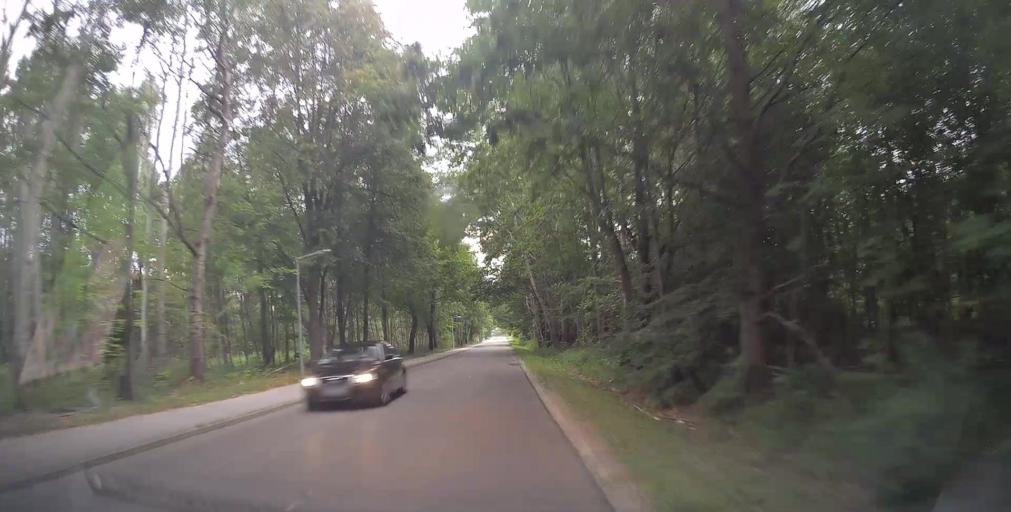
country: PL
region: Masovian Voivodeship
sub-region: Powiat bialobrzeski
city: Bialobrzegi
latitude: 51.6366
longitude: 20.9537
